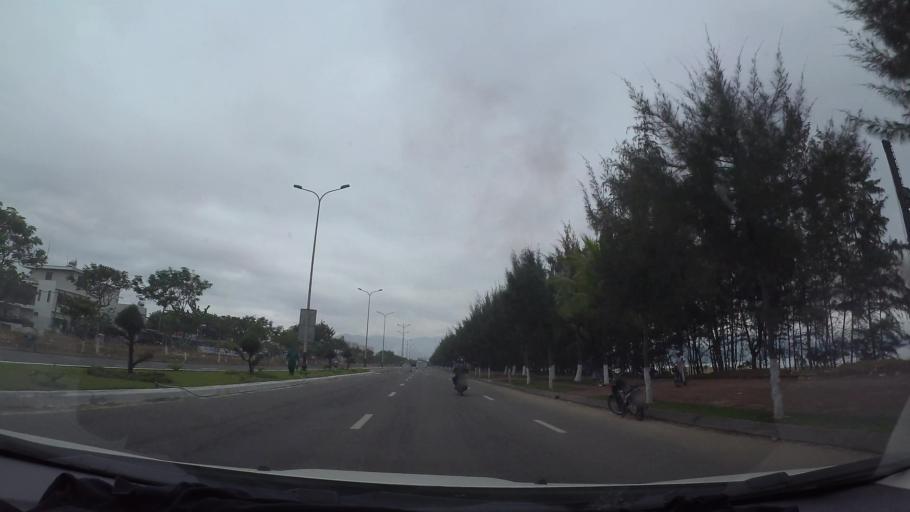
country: VN
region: Da Nang
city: Lien Chieu
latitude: 16.1046
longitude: 108.1371
